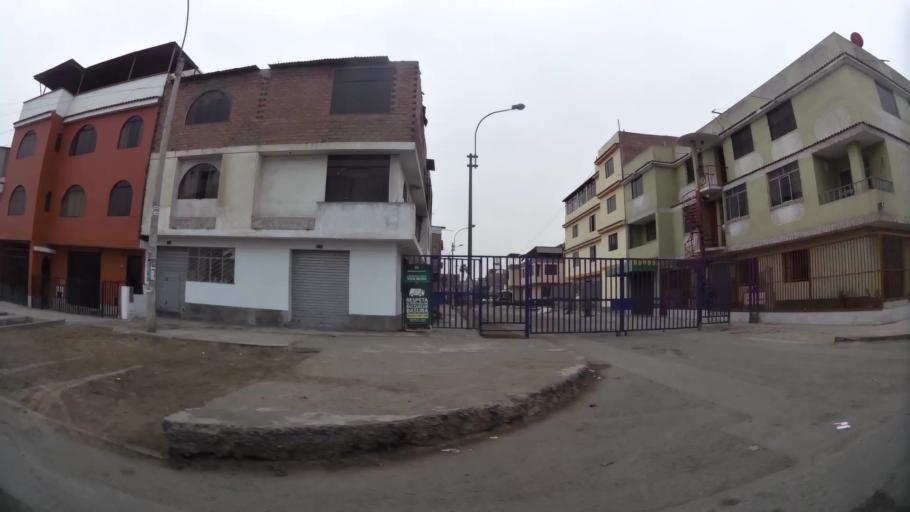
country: PE
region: Lima
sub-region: Lima
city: Surco
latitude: -12.1710
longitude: -76.9695
